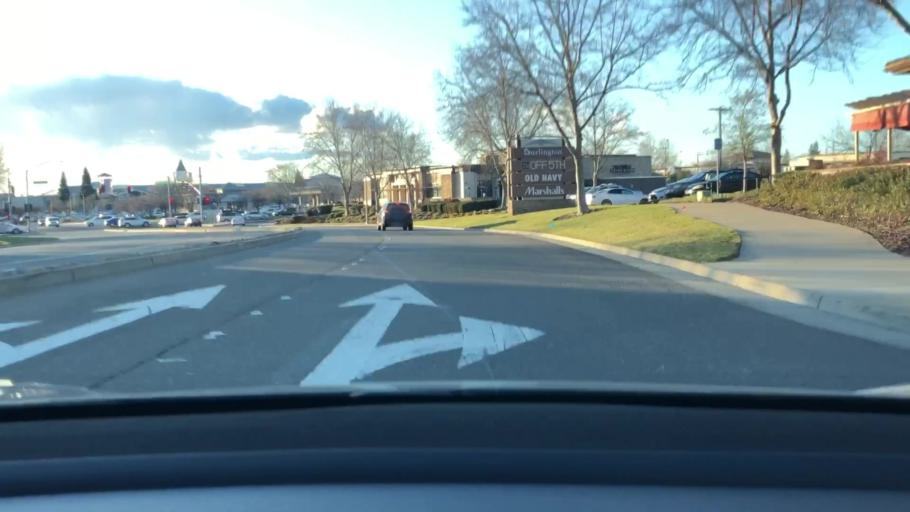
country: US
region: California
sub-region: Placer County
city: Roseville
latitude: 38.7719
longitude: -121.2640
